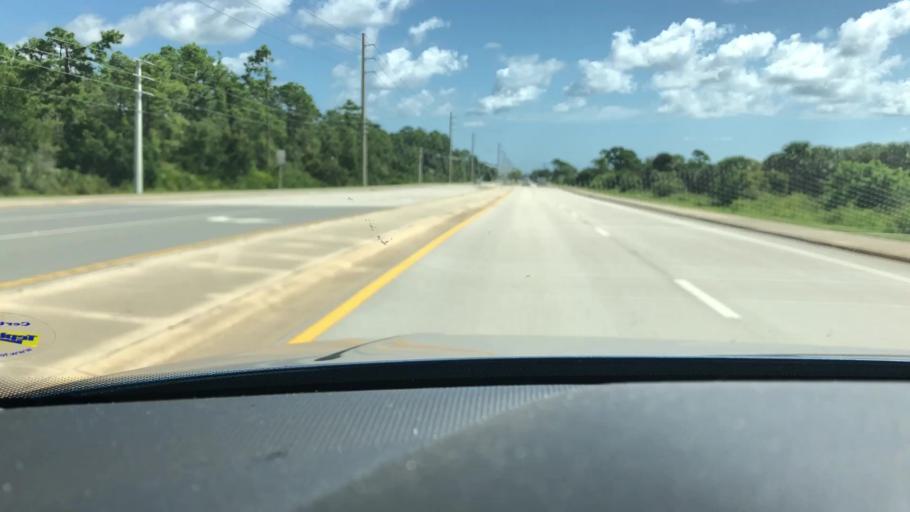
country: US
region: Florida
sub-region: Volusia County
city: Edgewater
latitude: 28.9632
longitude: -80.9213
